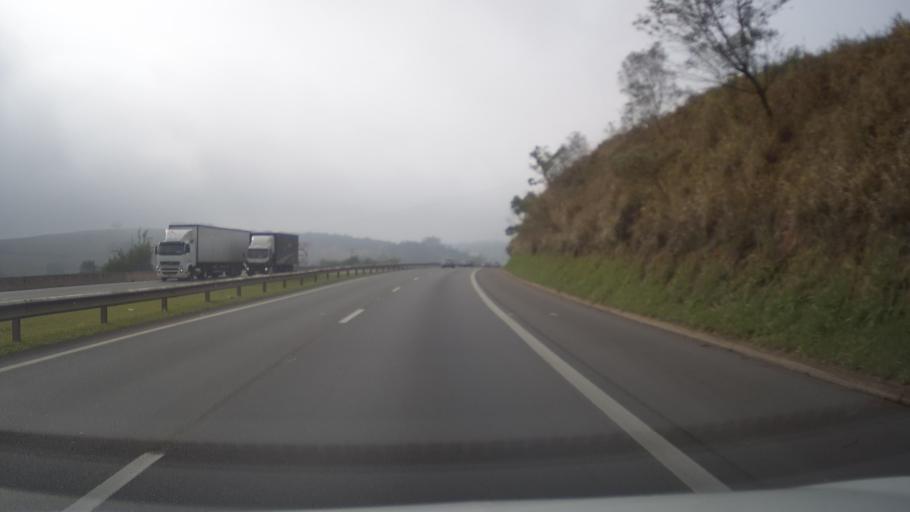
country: BR
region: Sao Paulo
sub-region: Itatiba
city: Itatiba
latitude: -23.0196
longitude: -46.7545
